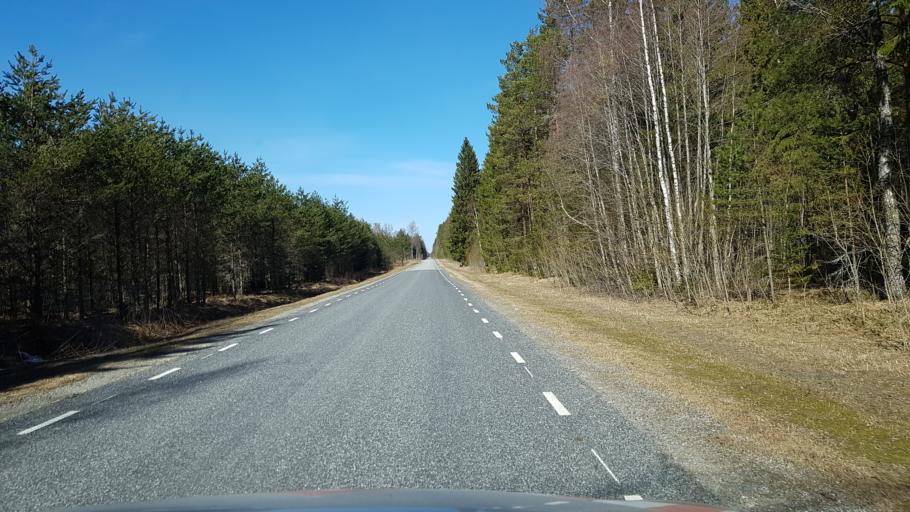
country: EE
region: Laeaene-Virumaa
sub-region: Vinni vald
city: Vinni
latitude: 59.1413
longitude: 26.5241
